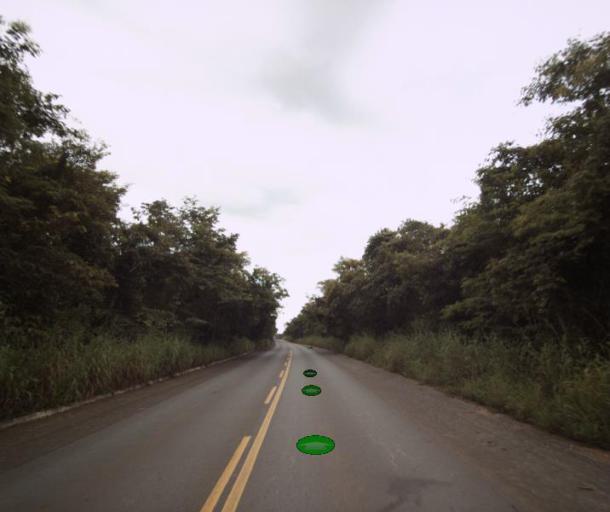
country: BR
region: Goias
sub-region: Niquelandia
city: Niquelandia
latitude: -14.5135
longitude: -48.5195
